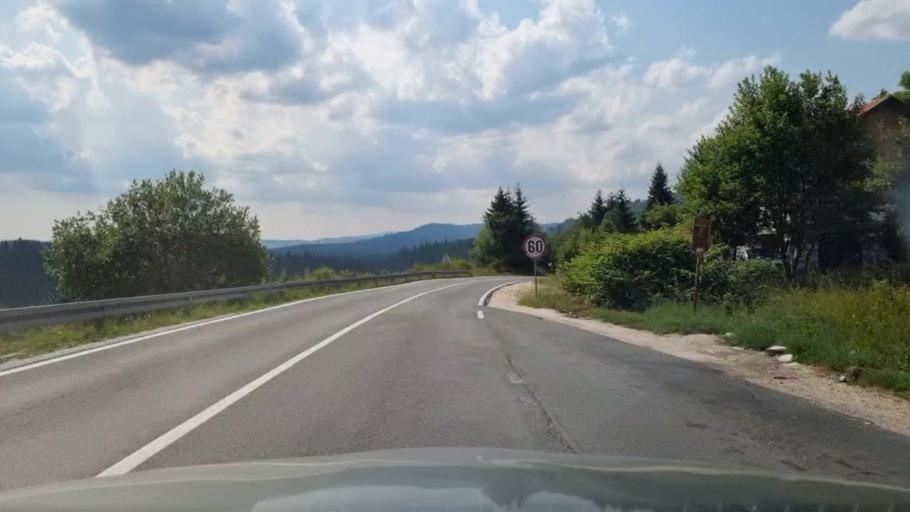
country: BA
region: Federation of Bosnia and Herzegovina
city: Olovo
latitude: 44.0785
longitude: 18.5280
